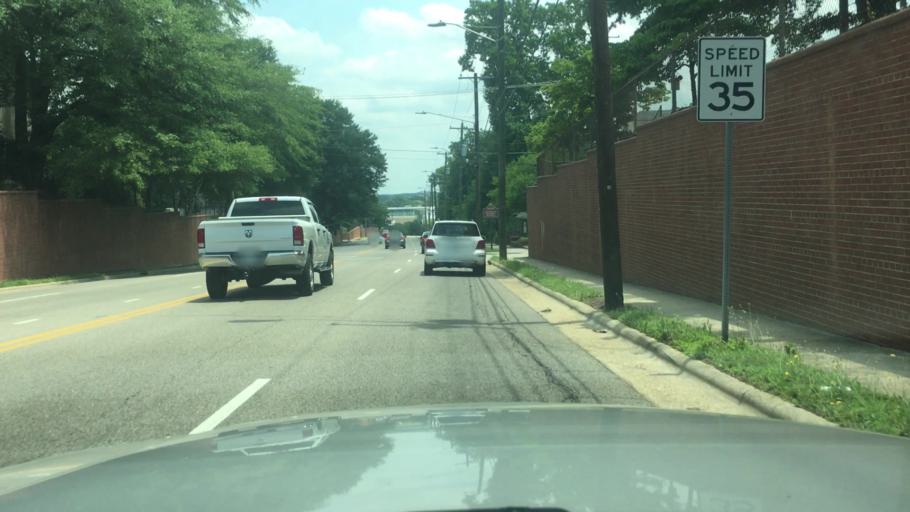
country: US
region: North Carolina
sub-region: Cumberland County
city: Fayetteville
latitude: 35.0559
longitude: -78.8913
